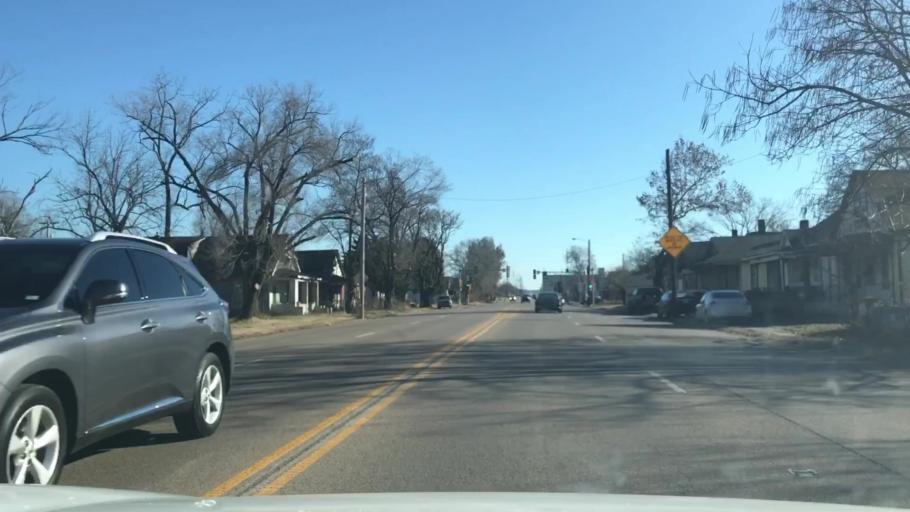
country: US
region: Illinois
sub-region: Saint Clair County
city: Alorton
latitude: 38.6065
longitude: -90.1357
